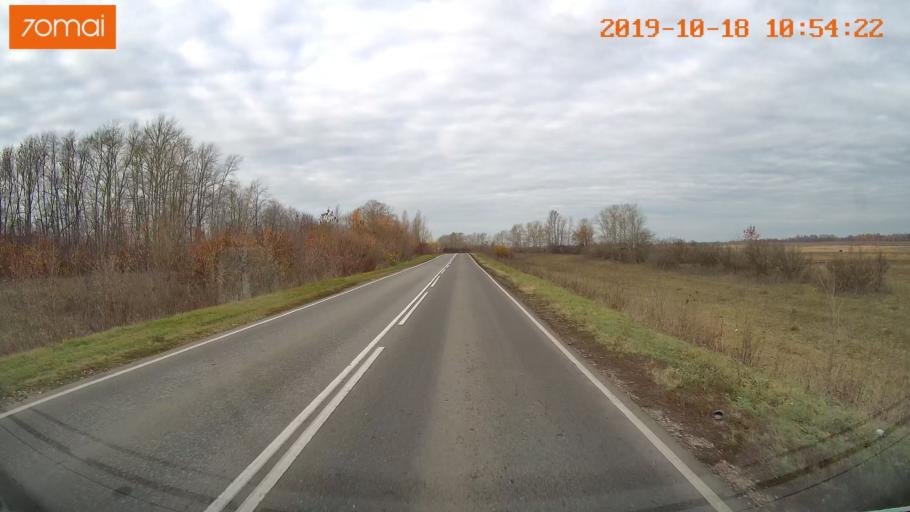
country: RU
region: Tula
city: Yepifan'
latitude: 53.7884
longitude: 38.6193
